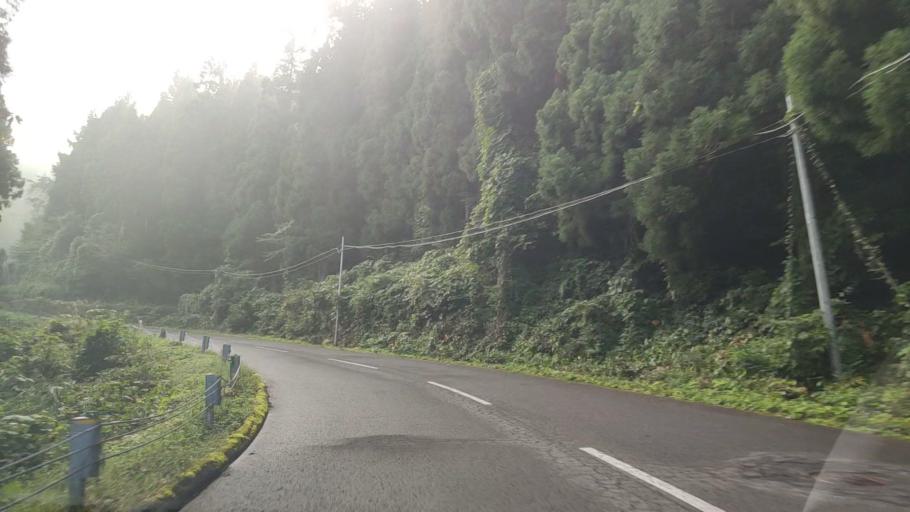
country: JP
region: Nagano
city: Iiyama
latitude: 36.8222
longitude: 138.4152
